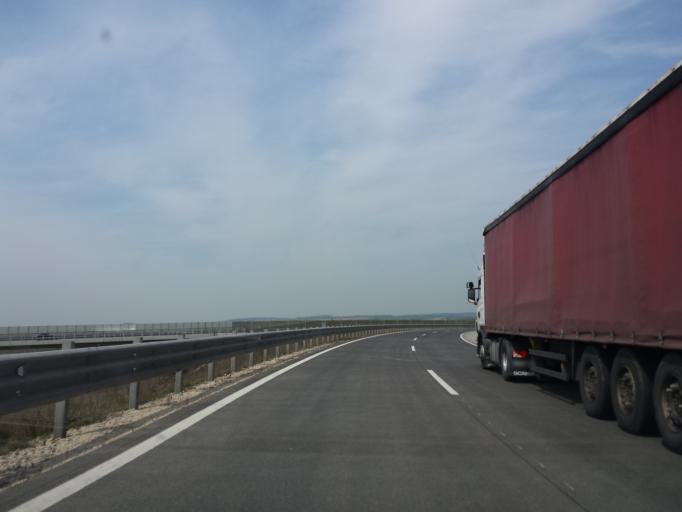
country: AT
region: Lower Austria
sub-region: Politischer Bezirk Mistelbach
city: Grossebersdorf
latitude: 48.3497
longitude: 16.4836
